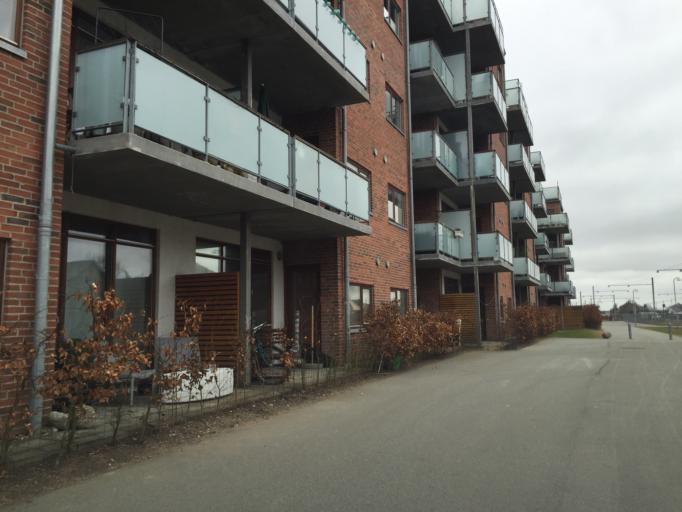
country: DK
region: Capital Region
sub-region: Hillerod Kommune
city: Hillerod
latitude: 55.9324
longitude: 12.3133
